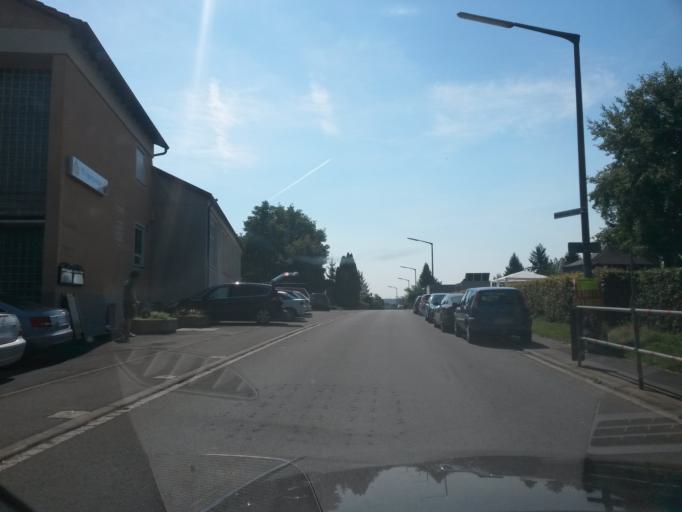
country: DE
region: Bavaria
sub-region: Regierungsbezirk Unterfranken
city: Estenfeld
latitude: 49.8332
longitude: 9.9971
